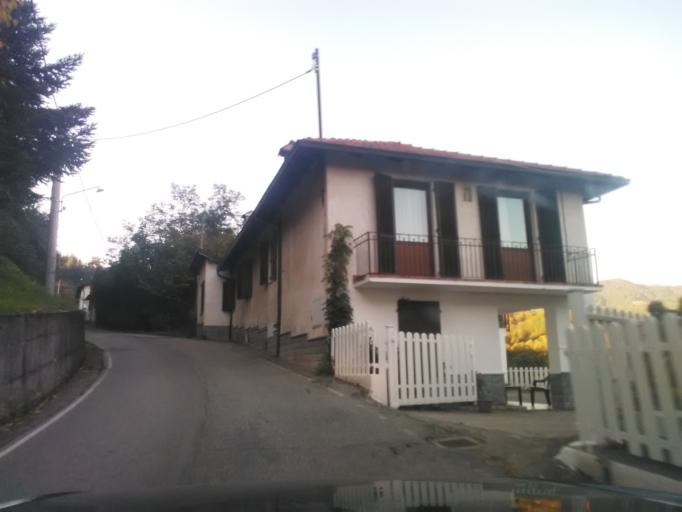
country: IT
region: Piedmont
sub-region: Provincia di Vercelli
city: Borgosesia
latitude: 45.7211
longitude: 8.2807
